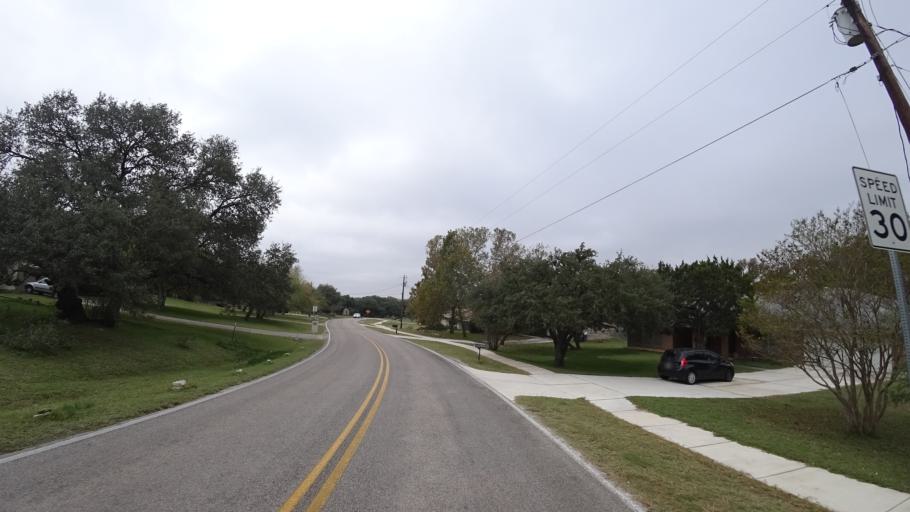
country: US
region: Texas
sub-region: Travis County
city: Barton Creek
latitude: 30.2243
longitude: -97.8993
